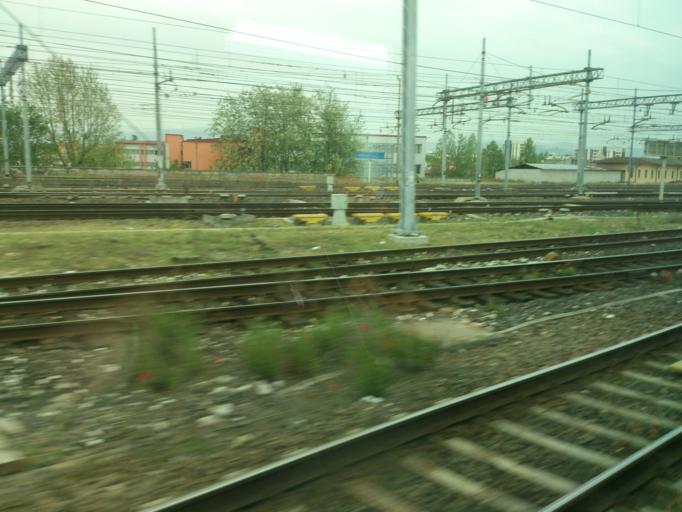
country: IT
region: Veneto
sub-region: Provincia di Verona
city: Verona
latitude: 45.4258
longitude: 10.9718
